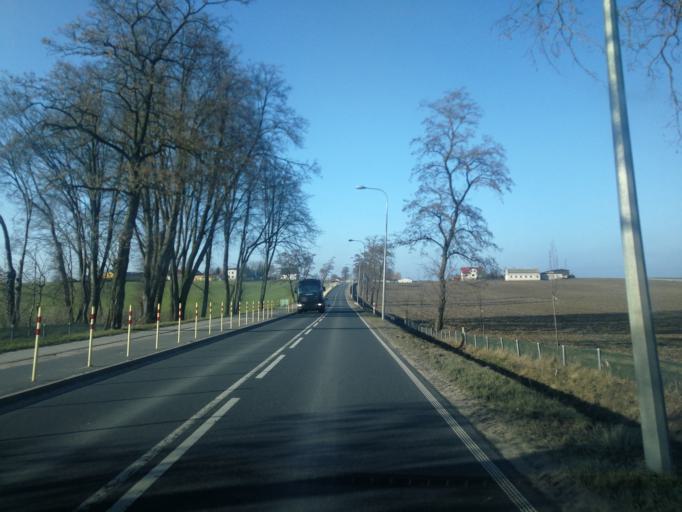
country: PL
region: Warmian-Masurian Voivodeship
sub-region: Powiat ilawski
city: Lubawa
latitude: 53.4606
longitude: 19.7756
